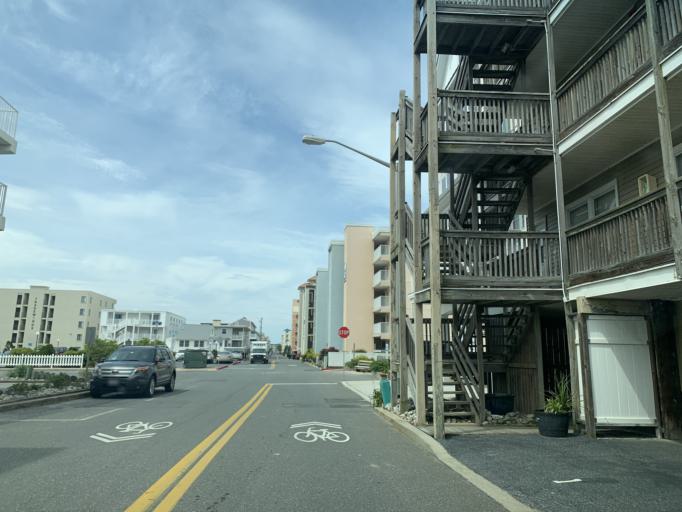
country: US
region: Delaware
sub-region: Sussex County
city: Bethany Beach
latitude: 38.4428
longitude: -75.0512
